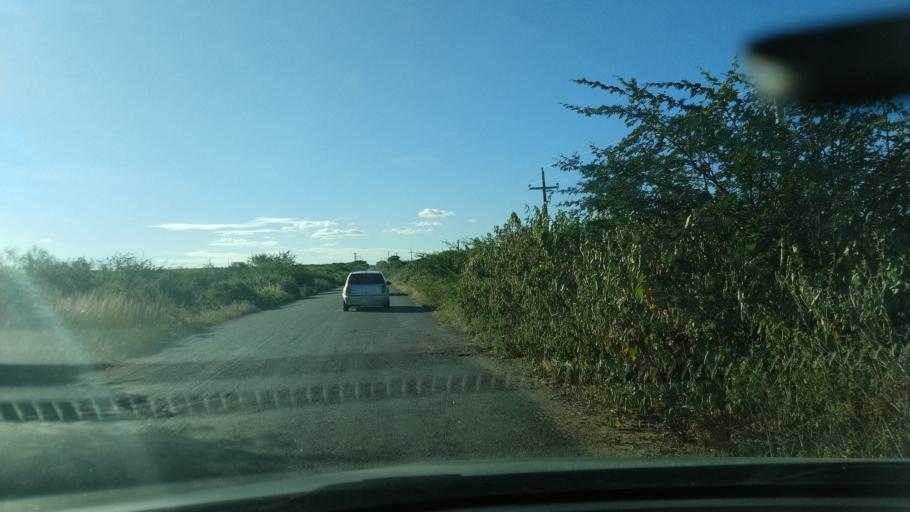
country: BR
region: Rio Grande do Norte
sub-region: Sao Jose Do Campestre
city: Sao Jose do Campestre
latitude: -6.4128
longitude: -35.6513
